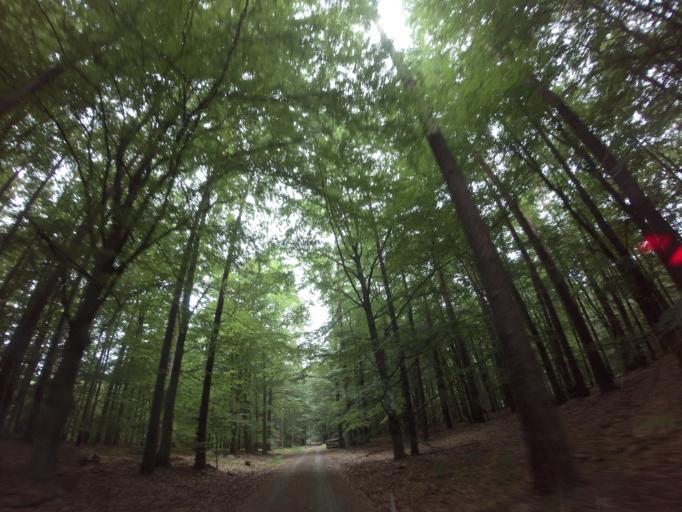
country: PL
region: Lubusz
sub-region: Powiat strzelecko-drezdenecki
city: Dobiegniew
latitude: 53.0494
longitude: 15.7955
